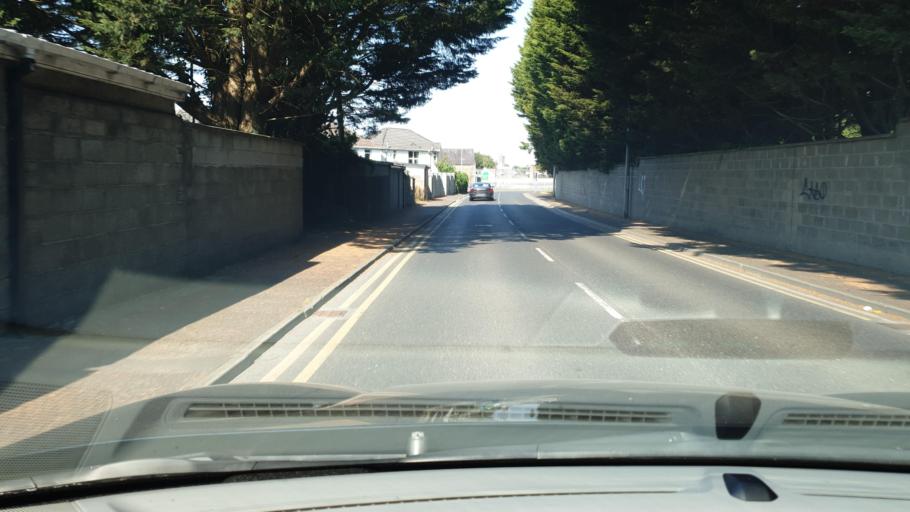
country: IE
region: Leinster
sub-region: An Mhi
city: Navan
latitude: 53.6466
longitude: -6.6922
